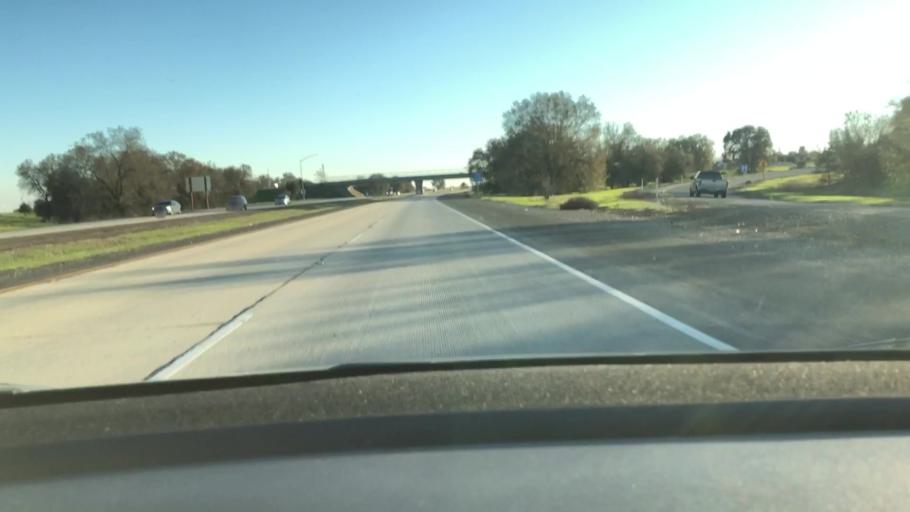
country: US
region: California
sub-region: Yolo County
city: Woodland
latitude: 38.6659
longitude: -121.7514
